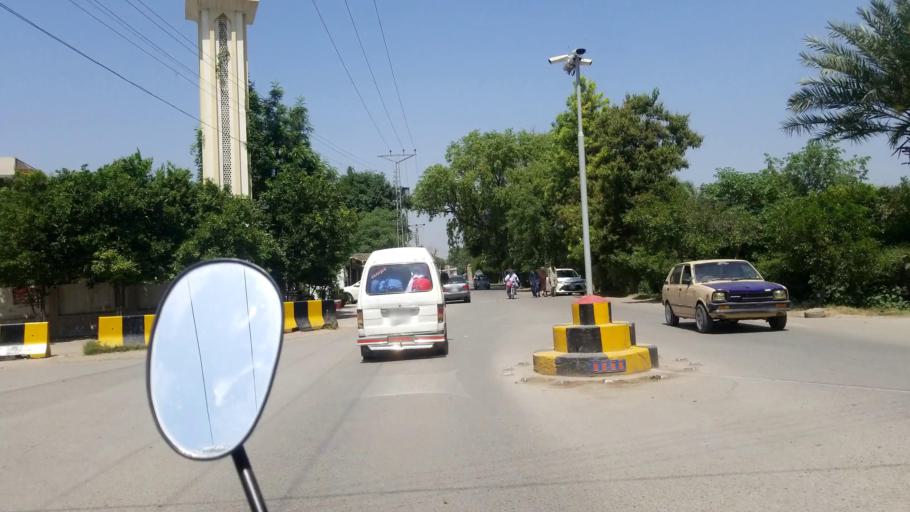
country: PK
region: Khyber Pakhtunkhwa
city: Peshawar
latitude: 34.0122
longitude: 71.4868
